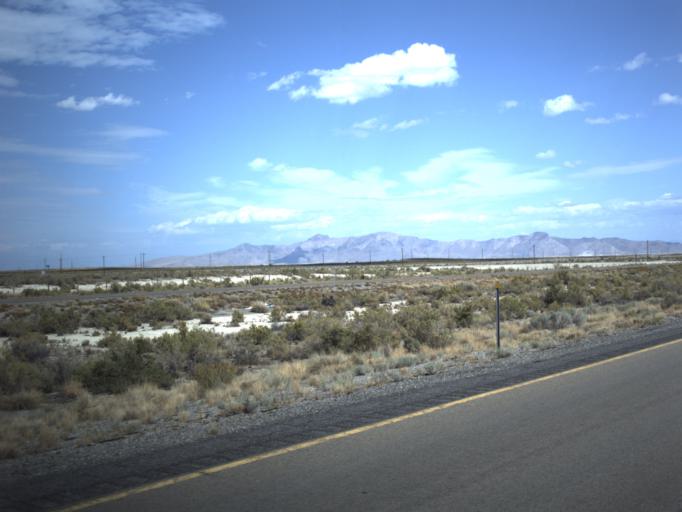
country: US
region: Utah
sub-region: Tooele County
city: Grantsville
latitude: 40.7542
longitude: -112.7386
